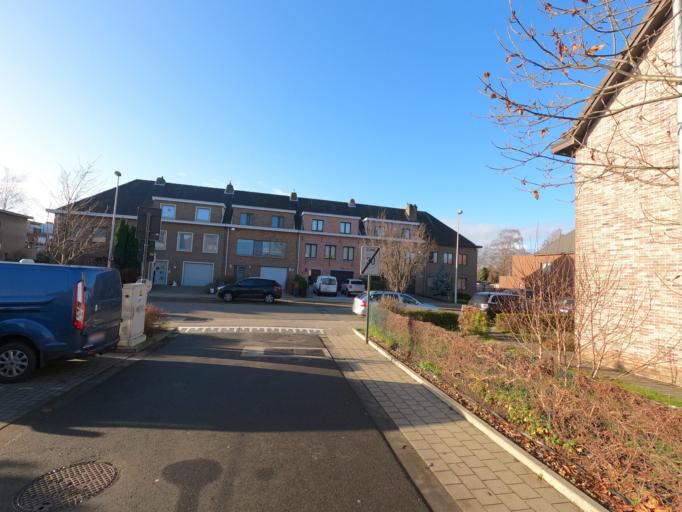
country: BE
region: Flanders
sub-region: Provincie Antwerpen
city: Wijnegem
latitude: 51.2271
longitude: 4.5133
